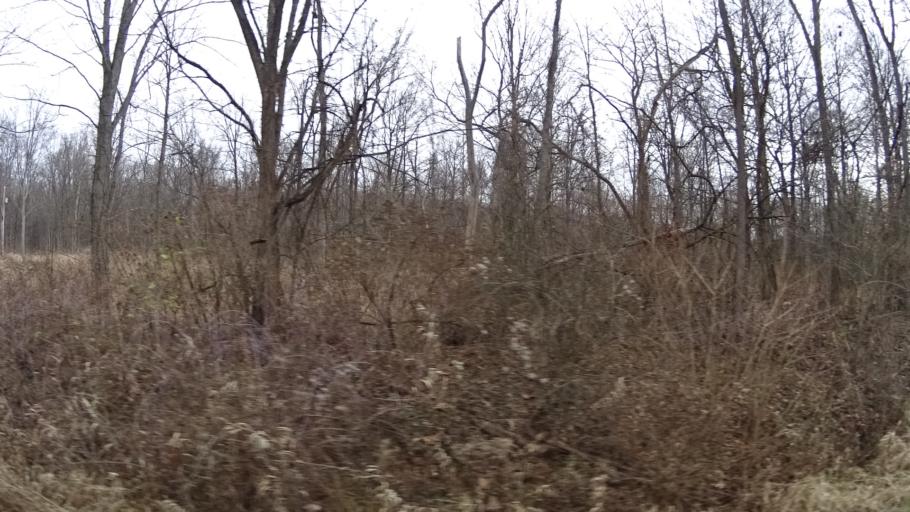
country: US
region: Ohio
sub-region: Lorain County
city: Wellington
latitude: 41.1763
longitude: -82.2425
